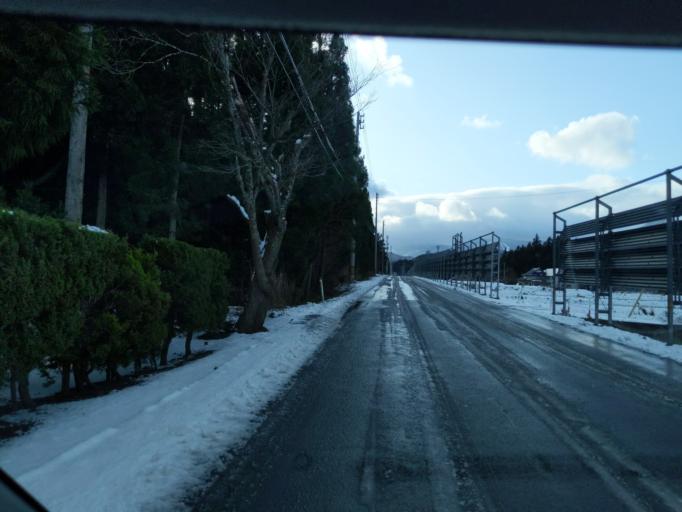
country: JP
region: Iwate
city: Kitakami
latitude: 39.2445
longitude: 140.9958
